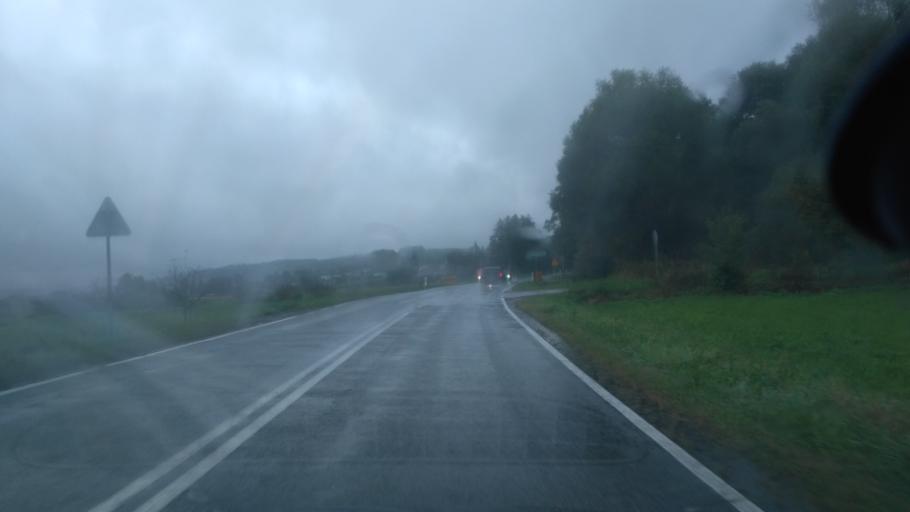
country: PL
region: Subcarpathian Voivodeship
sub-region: Powiat ropczycko-sedziszowski
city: Niedzwiada
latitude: 49.9877
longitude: 21.5614
